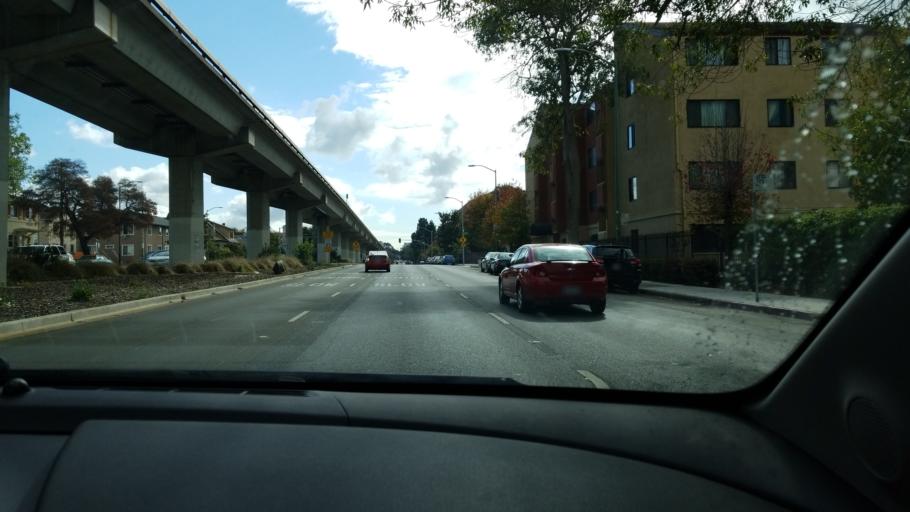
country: US
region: California
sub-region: Alameda County
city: Emeryville
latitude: 37.8458
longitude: -122.2712
